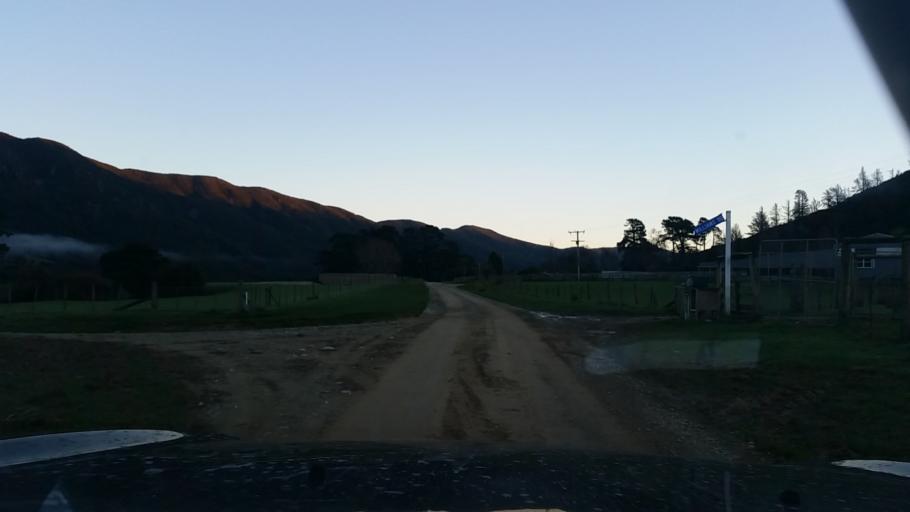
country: NZ
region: Marlborough
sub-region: Marlborough District
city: Picton
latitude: -41.1553
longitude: 174.1297
